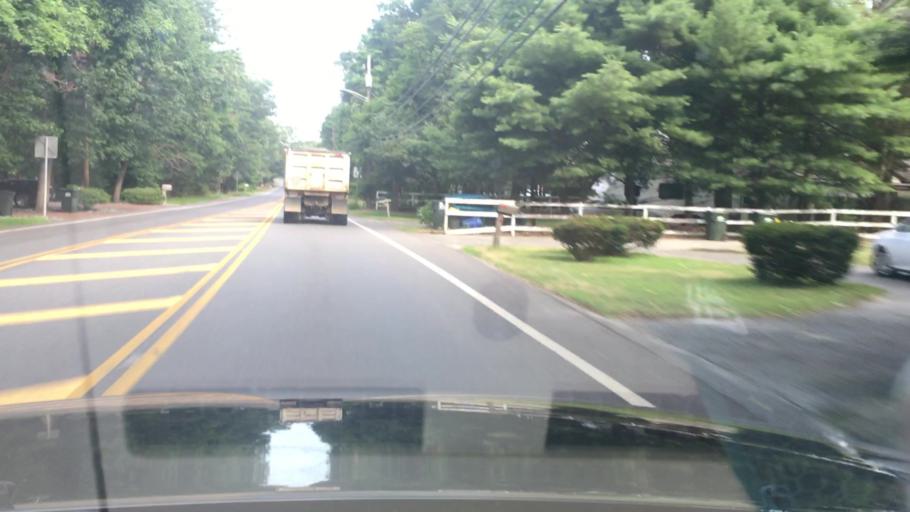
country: US
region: New Jersey
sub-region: Ocean County
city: Vista Center
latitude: 40.1506
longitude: -74.3993
